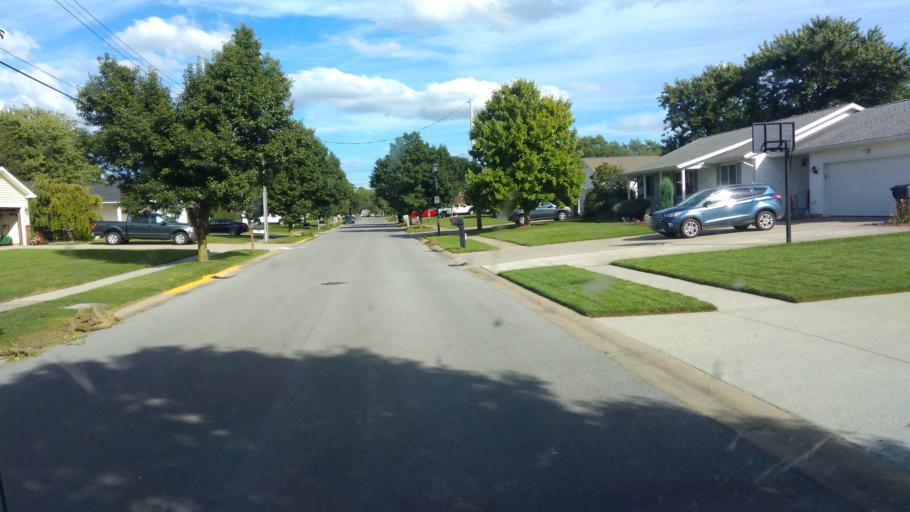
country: US
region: Ohio
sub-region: Sandusky County
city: Clyde
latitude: 41.2937
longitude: -82.9875
